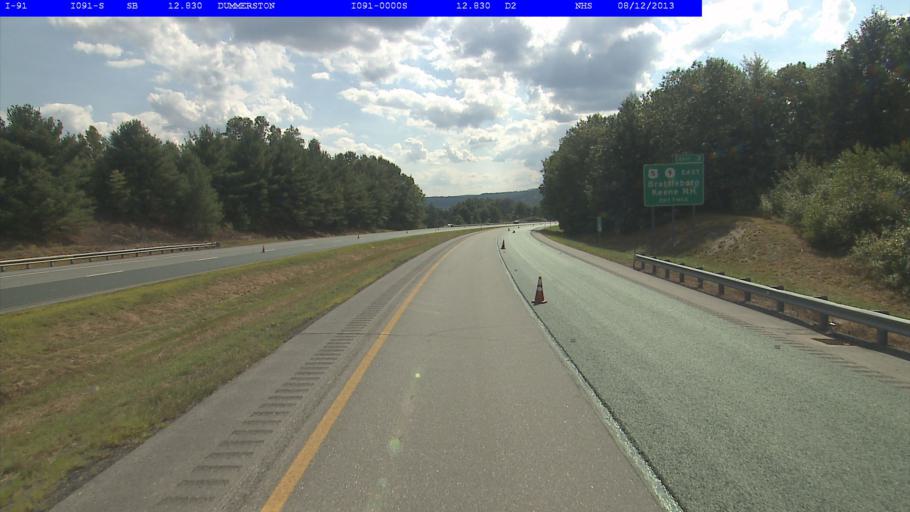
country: US
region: Vermont
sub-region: Windham County
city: Brattleboro
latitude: 42.8971
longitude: -72.5406
